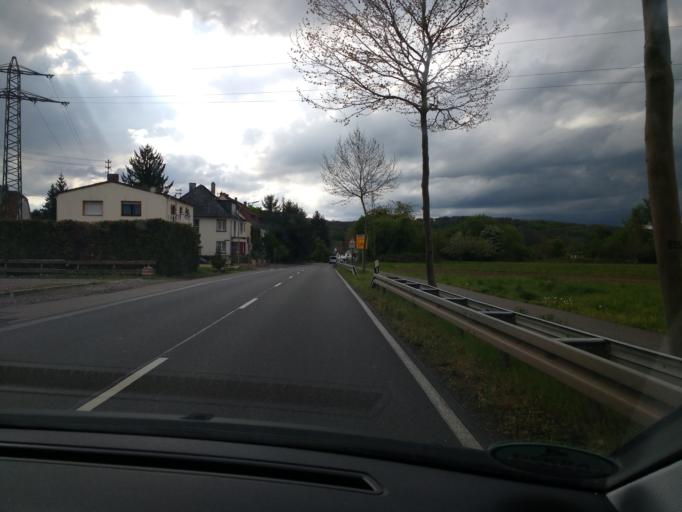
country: FR
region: Lorraine
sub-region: Departement de la Moselle
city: Sarreguemines
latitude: 49.1249
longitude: 7.0522
